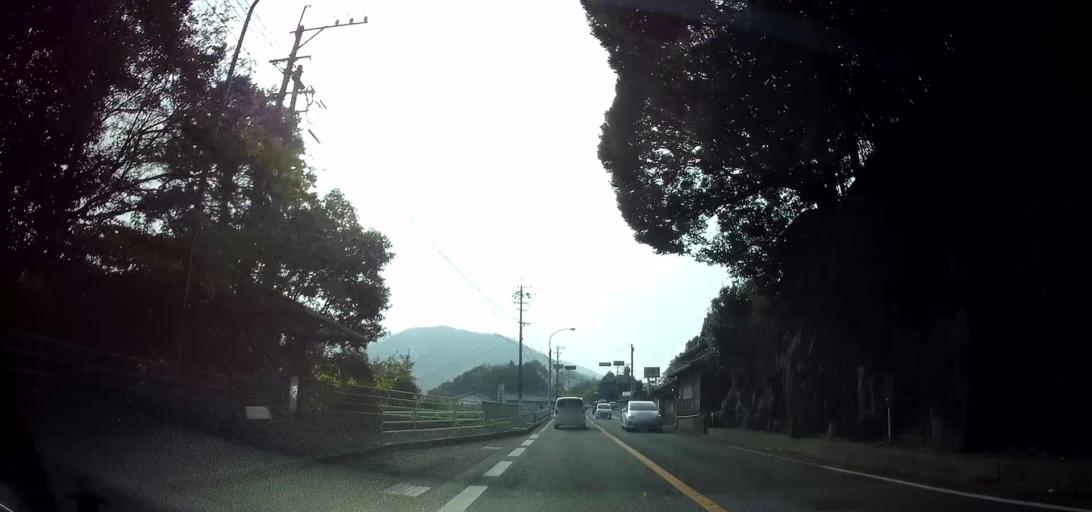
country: JP
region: Nagasaki
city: Shimabara
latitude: 32.7723
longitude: 130.2141
